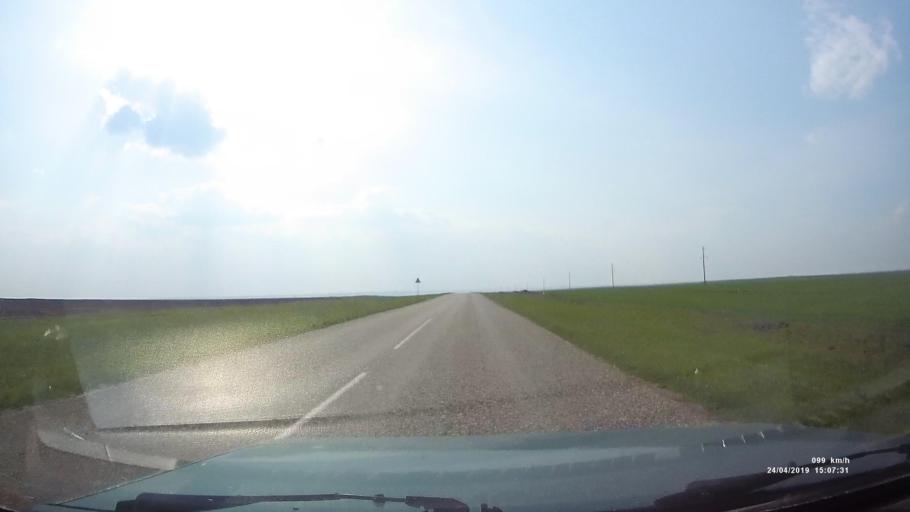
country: RU
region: Rostov
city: Remontnoye
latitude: 46.5597
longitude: 43.4031
